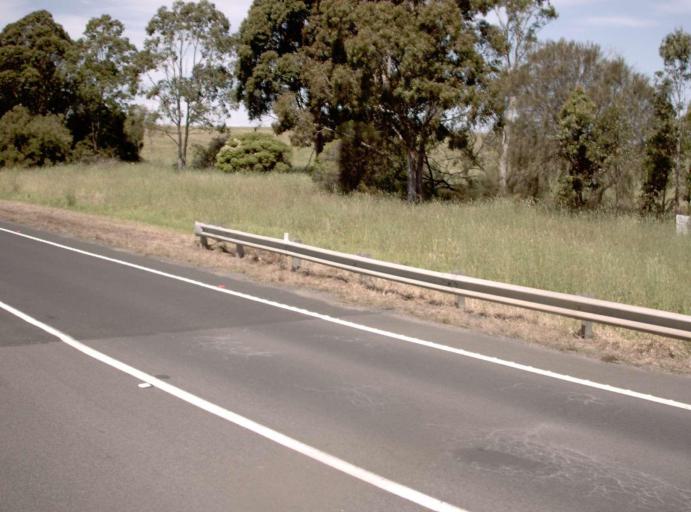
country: AU
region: Victoria
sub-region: Wellington
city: Heyfield
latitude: -38.1072
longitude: 146.8976
